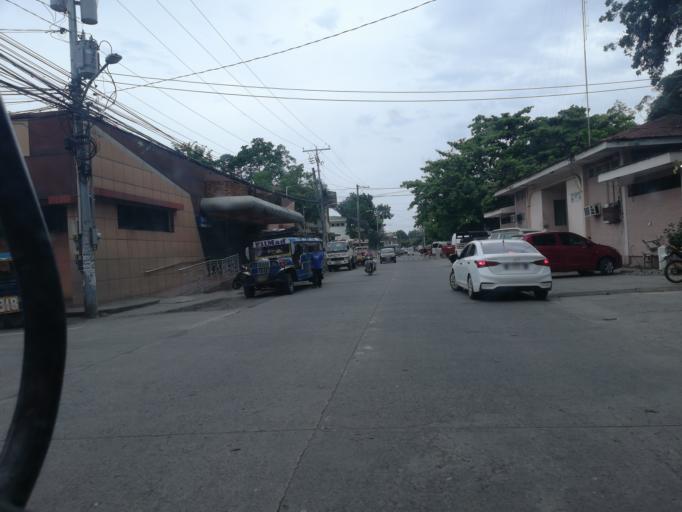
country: PH
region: Central Visayas
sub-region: Province of Negros Oriental
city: Dumaguete
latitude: 9.3061
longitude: 123.3087
